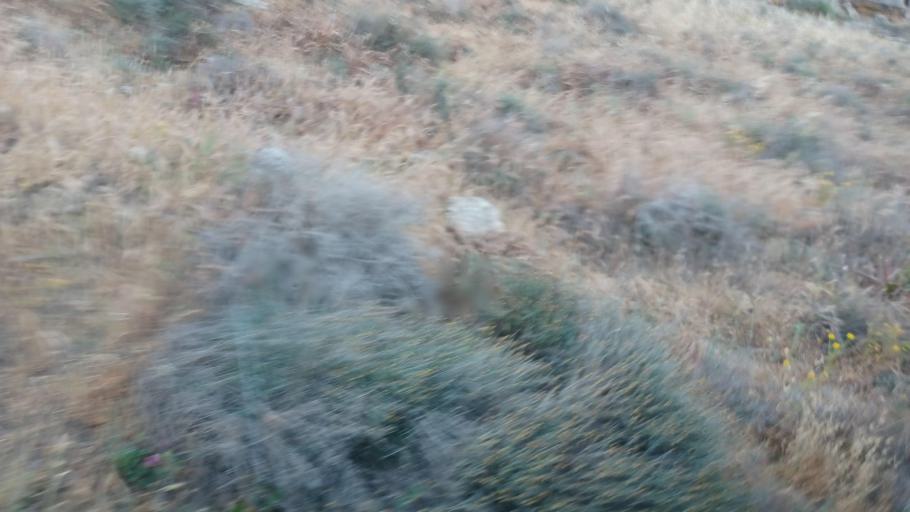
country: CY
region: Lefkosia
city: Kokkinotrimithia
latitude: 35.1724
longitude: 33.1605
